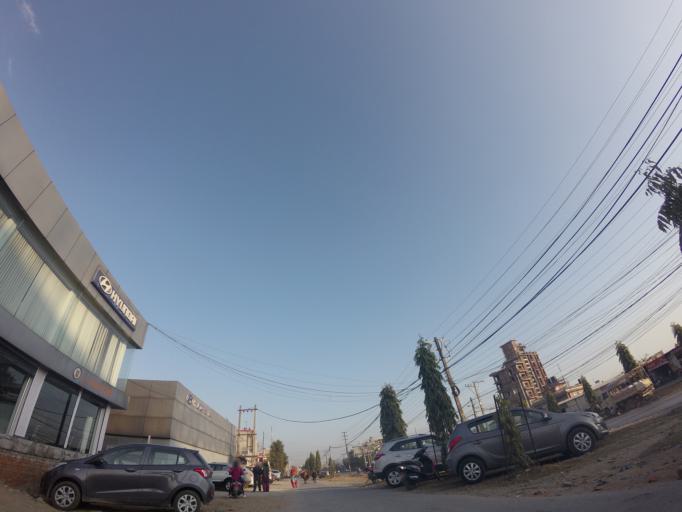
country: NP
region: Western Region
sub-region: Gandaki Zone
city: Pokhara
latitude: 28.2057
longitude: 83.9982
